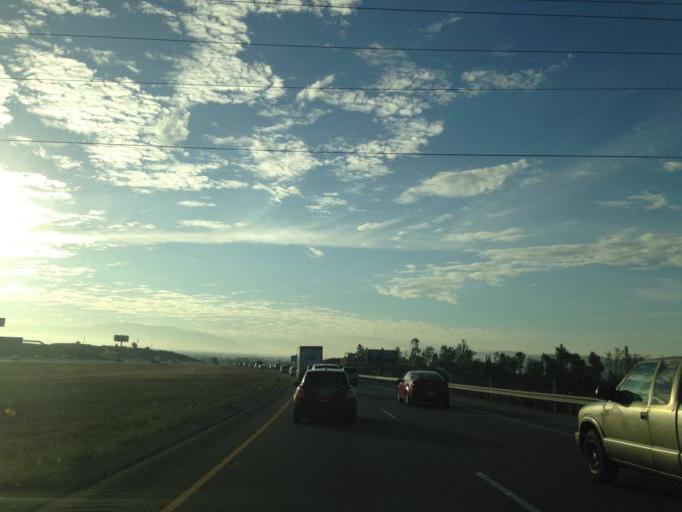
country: US
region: California
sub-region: Riverside County
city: Murrieta Hot Springs
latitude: 33.5456
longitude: -117.1801
